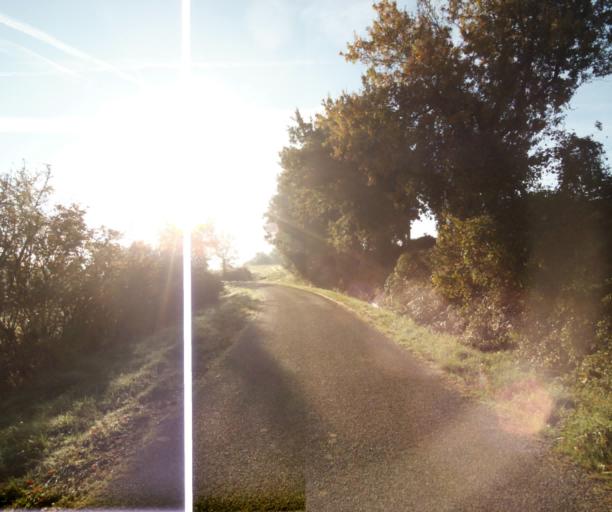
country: FR
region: Midi-Pyrenees
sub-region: Departement de la Haute-Garonne
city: Villemur-sur-Tarn
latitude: 43.8930
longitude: 1.4837
